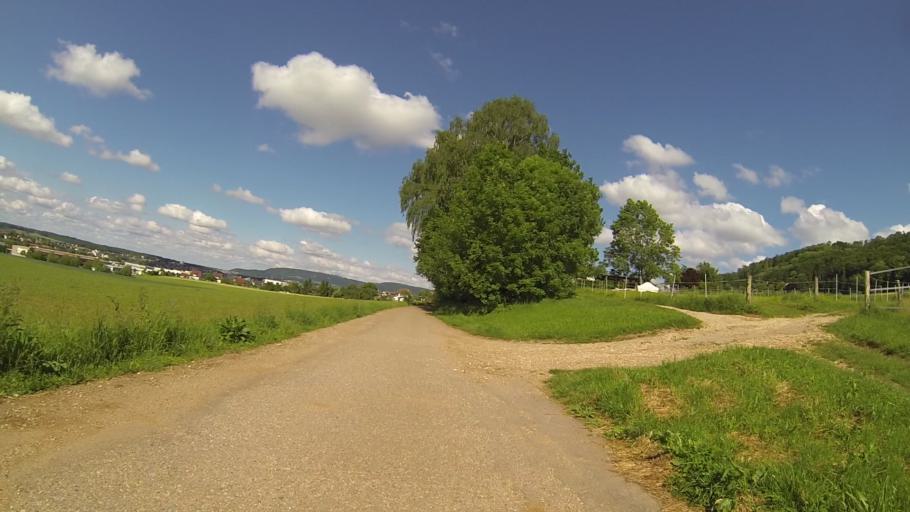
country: DE
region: Baden-Wuerttemberg
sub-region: Regierungsbezirk Stuttgart
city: Essingen
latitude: 48.8186
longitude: 10.0572
